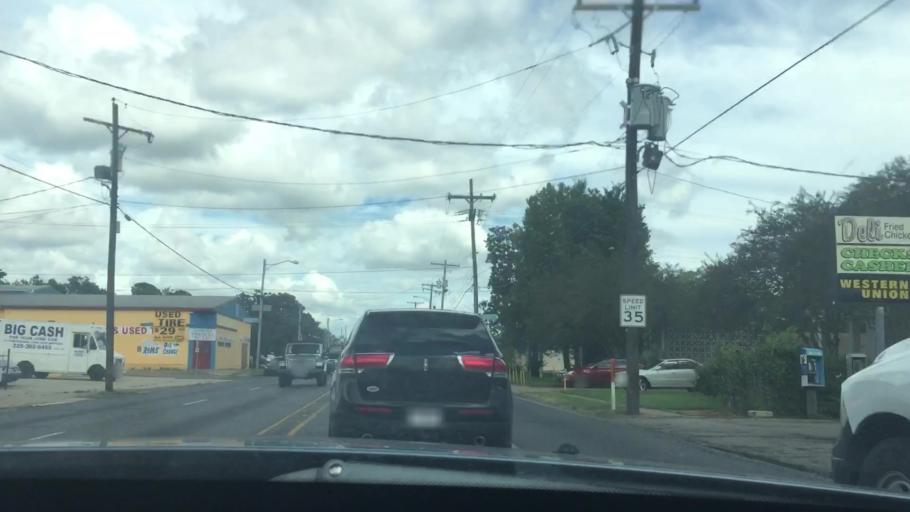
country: US
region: Louisiana
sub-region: East Baton Rouge Parish
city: Baton Rouge
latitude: 30.4499
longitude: -91.1671
